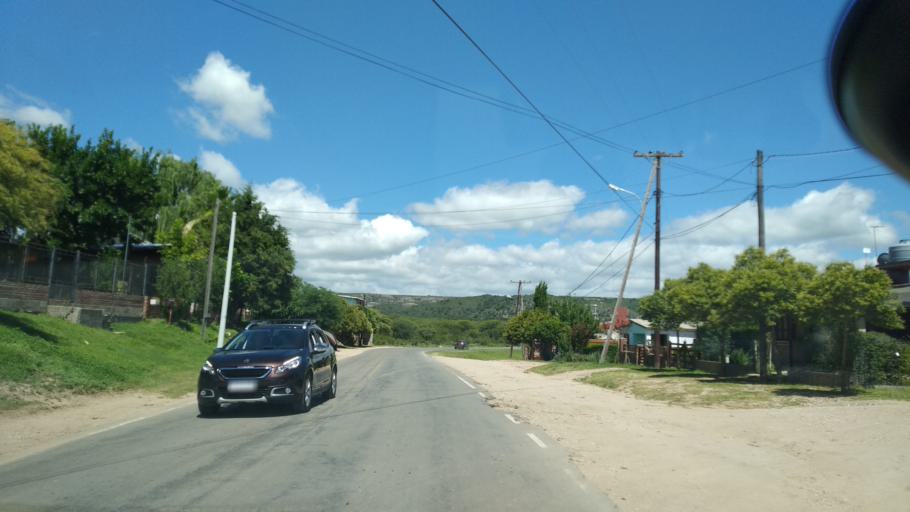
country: AR
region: Cordoba
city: Villa Cura Brochero
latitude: -31.7028
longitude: -65.0290
